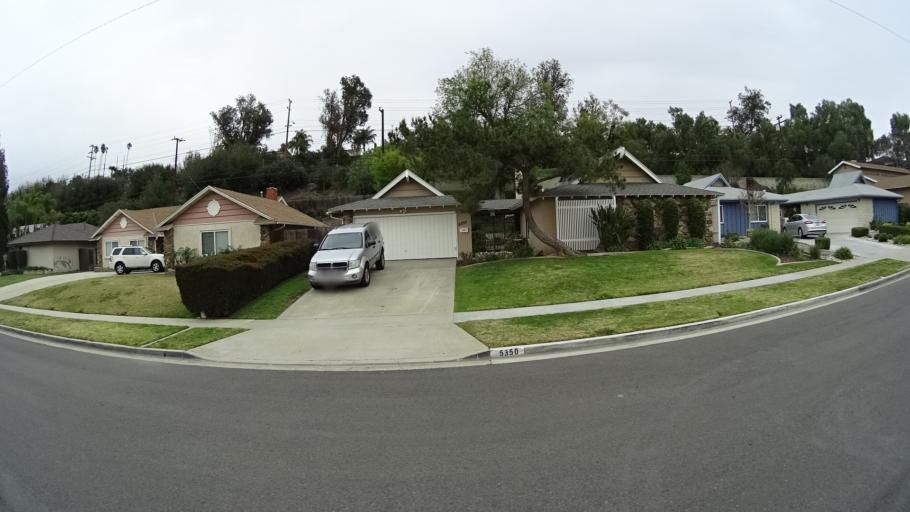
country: US
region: California
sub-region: Orange County
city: Yorba Linda
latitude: 33.8521
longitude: -117.7992
